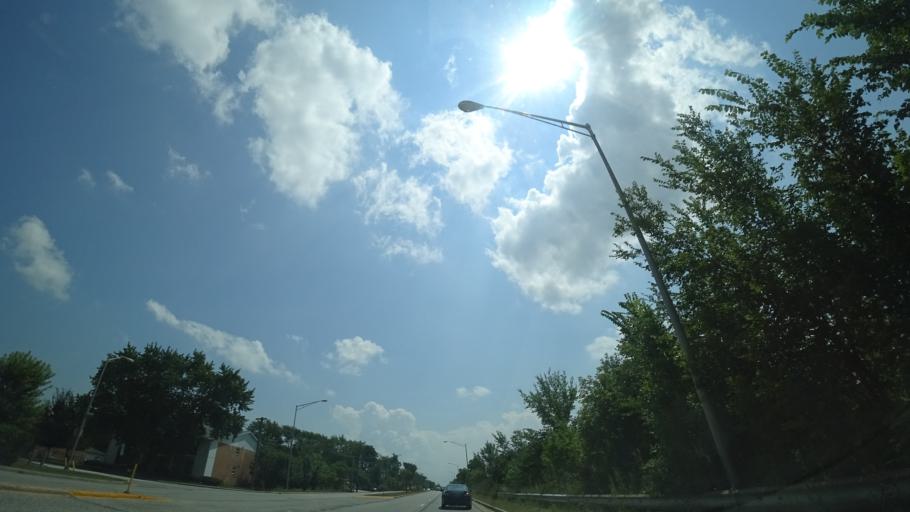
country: US
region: Illinois
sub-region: Cook County
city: Tinley Park
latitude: 41.5691
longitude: -87.7932
